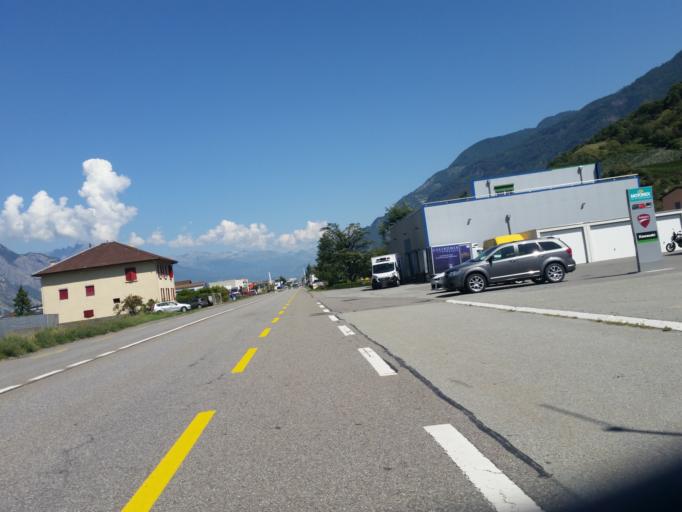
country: CH
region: Valais
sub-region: Martigny District
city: Saxon
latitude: 46.1414
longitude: 7.1584
